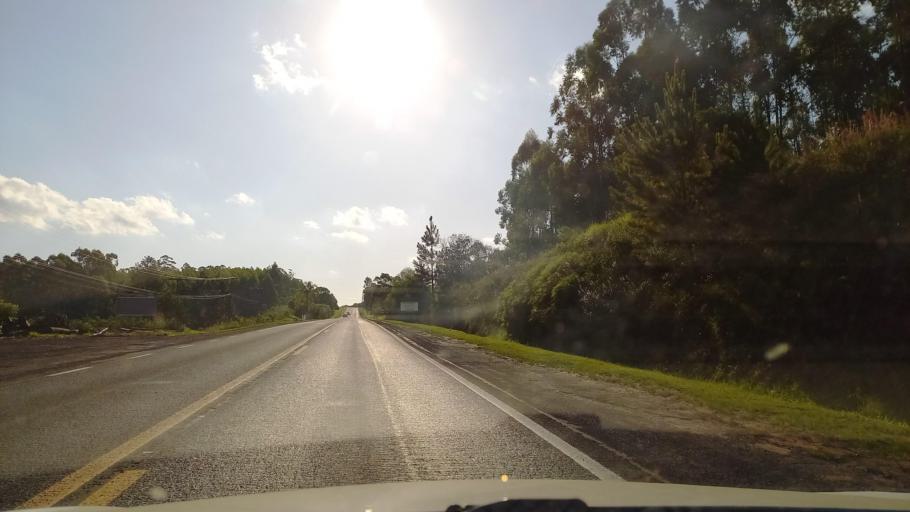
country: BR
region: Rio Grande do Sul
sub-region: Taquari
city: Taquari
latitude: -29.7073
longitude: -51.7866
